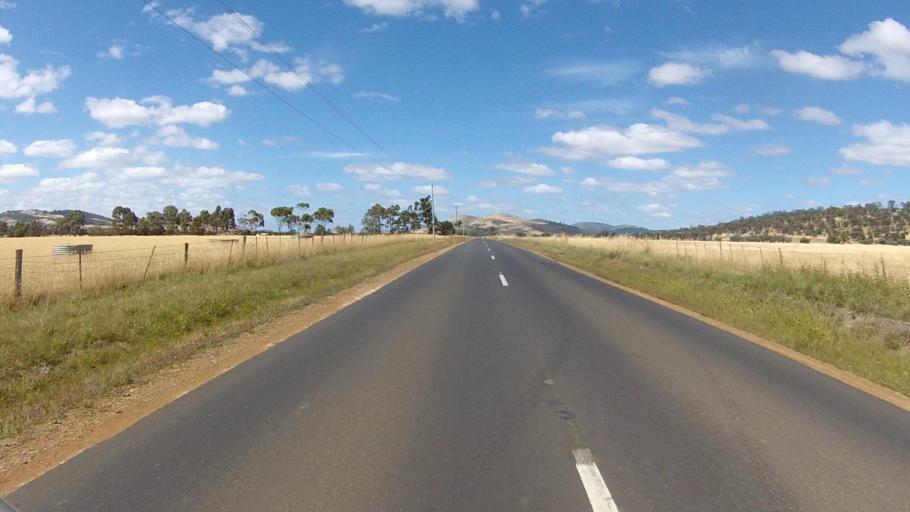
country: AU
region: Tasmania
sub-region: Clarence
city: Cambridge
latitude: -42.7085
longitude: 147.4298
